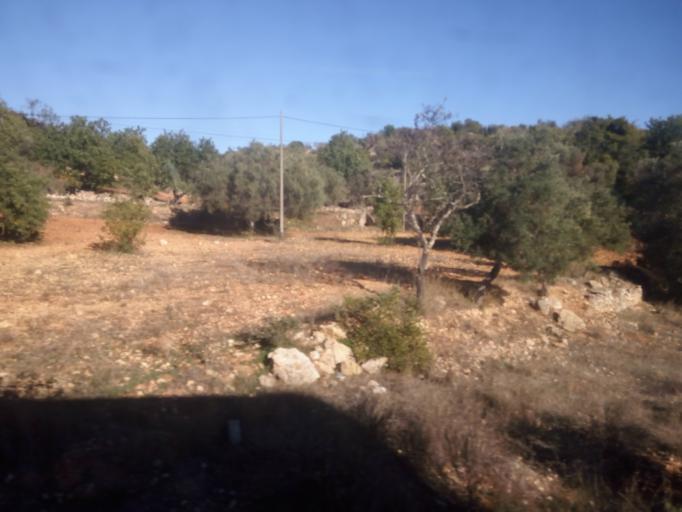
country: PT
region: Faro
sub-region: Albufeira
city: Ferreiras
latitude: 37.1579
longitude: -8.2503
